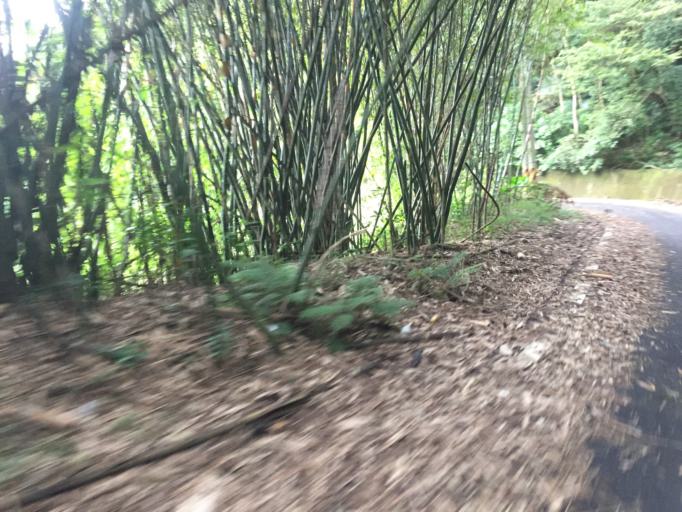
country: TW
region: Taiwan
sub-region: Hsinchu
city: Zhubei
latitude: 24.7879
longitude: 121.1559
